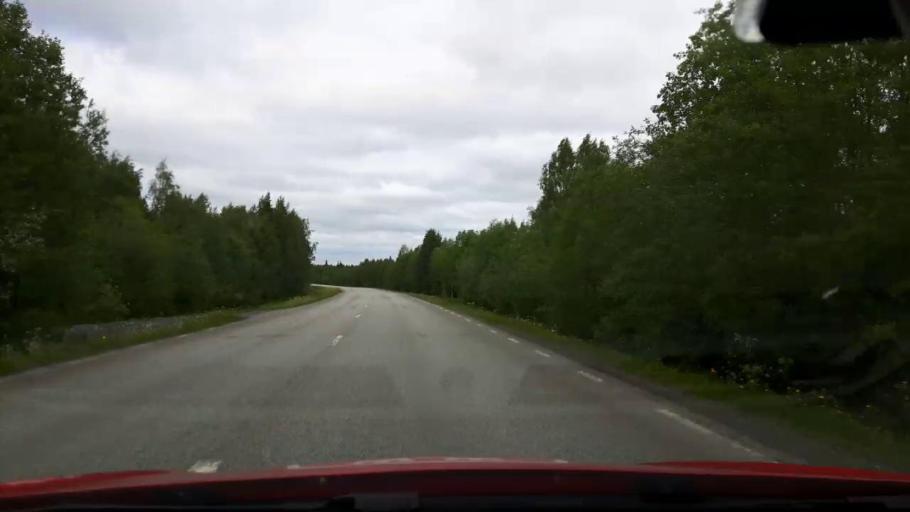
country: SE
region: Jaemtland
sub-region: Krokoms Kommun
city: Krokom
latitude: 63.3813
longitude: 14.5072
